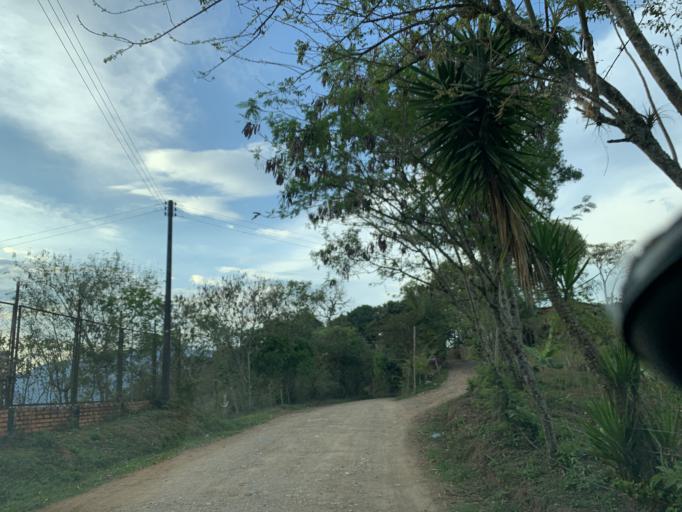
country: CO
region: Boyaca
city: Santana
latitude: 6.0827
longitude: -73.4944
